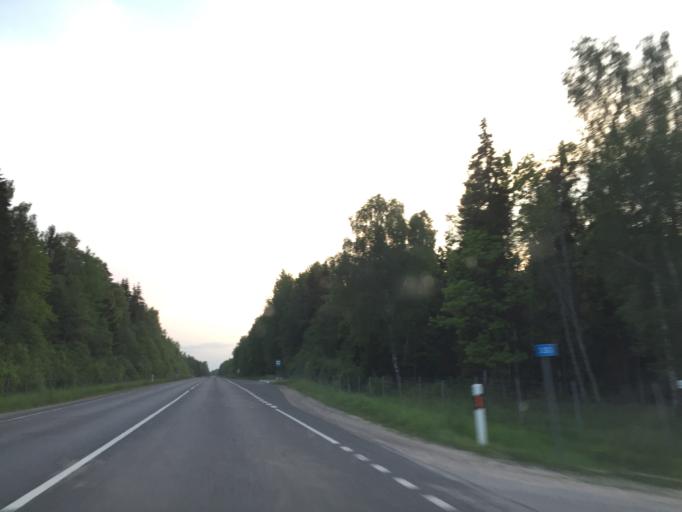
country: LT
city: Kursenai
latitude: 55.9998
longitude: 22.8198
